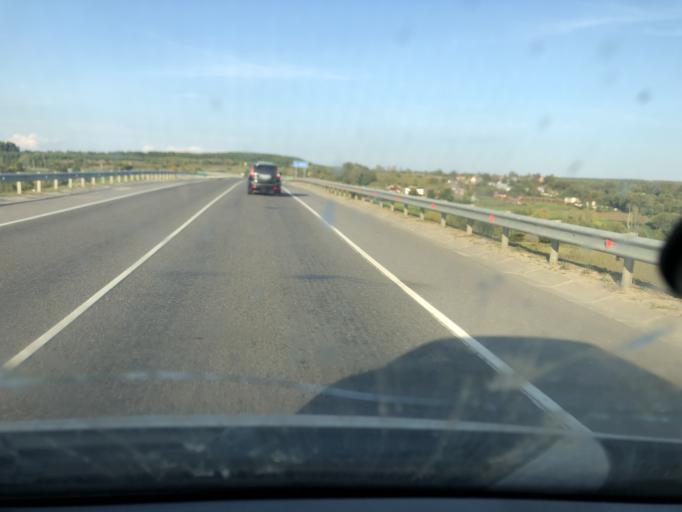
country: RU
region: Kaluga
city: Peremyshl'
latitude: 54.2913
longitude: 36.1728
